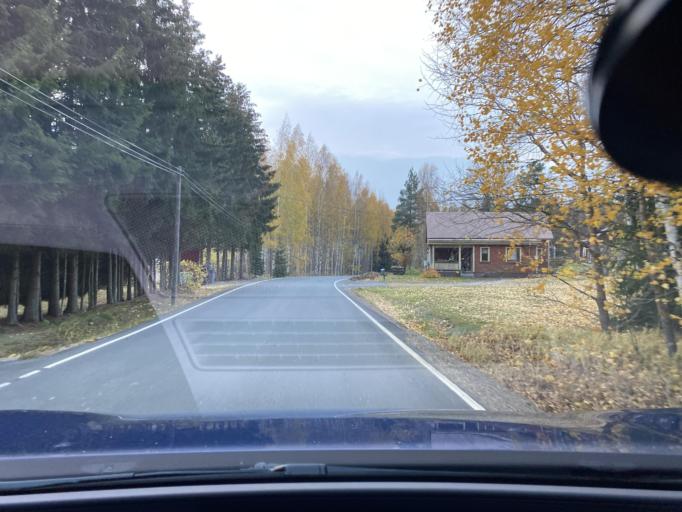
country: FI
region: Varsinais-Suomi
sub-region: Loimaa
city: Alastaro
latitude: 61.0883
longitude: 22.9131
